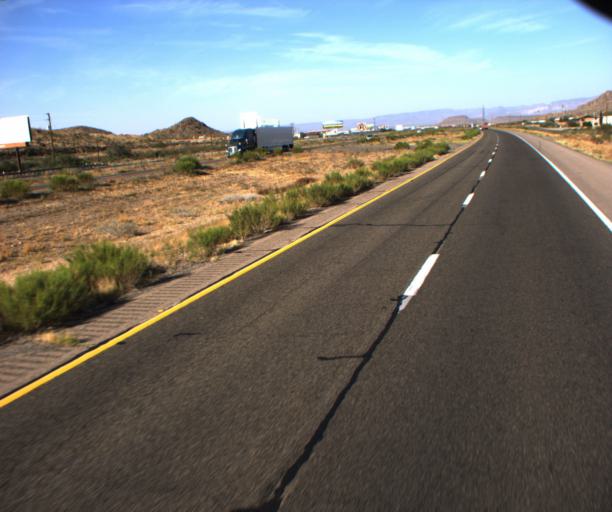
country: US
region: Arizona
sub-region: Mohave County
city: Kingman
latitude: 35.1596
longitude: -114.0802
